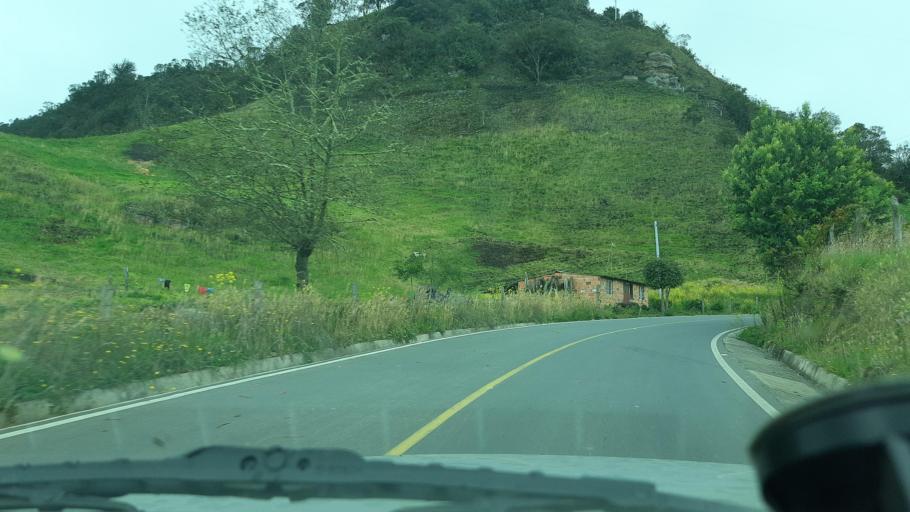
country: CO
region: Cundinamarca
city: Umbita
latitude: 5.2267
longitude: -73.4722
